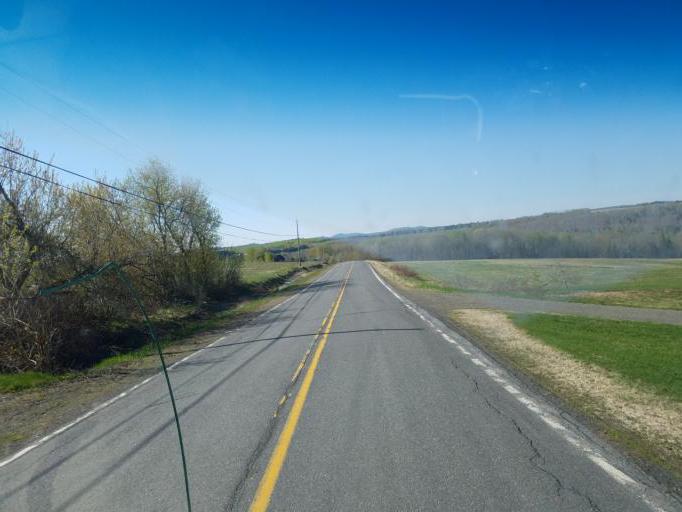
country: US
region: Maine
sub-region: Aroostook County
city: Caribou
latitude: 46.8625
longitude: -68.2086
